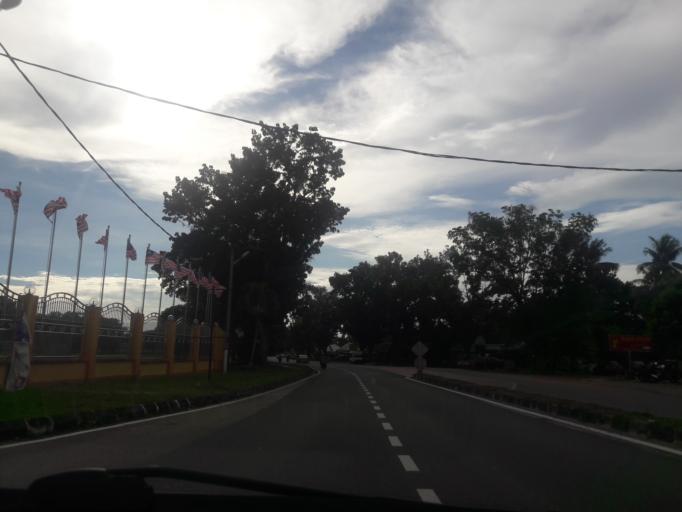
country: MY
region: Kedah
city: Sungai Petani
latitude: 5.6303
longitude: 100.5232
